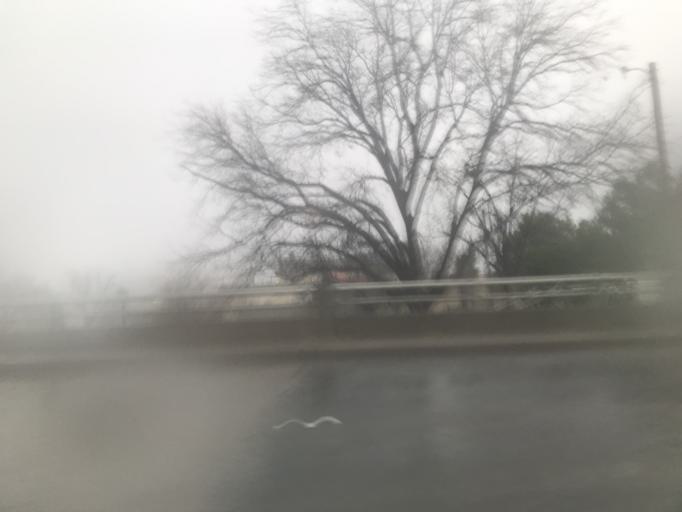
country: US
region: Texas
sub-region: Tom Green County
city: San Angelo
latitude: 31.4570
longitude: -100.4345
